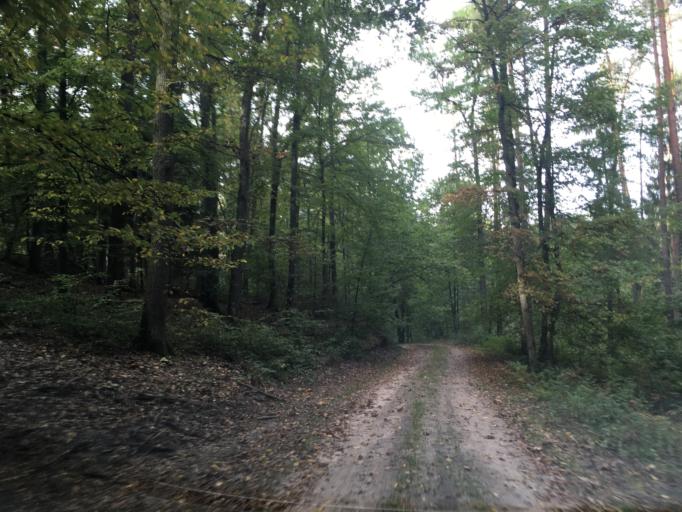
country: PL
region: Kujawsko-Pomorskie
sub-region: Powiat brodnicki
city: Gorzno
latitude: 53.2228
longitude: 19.7059
